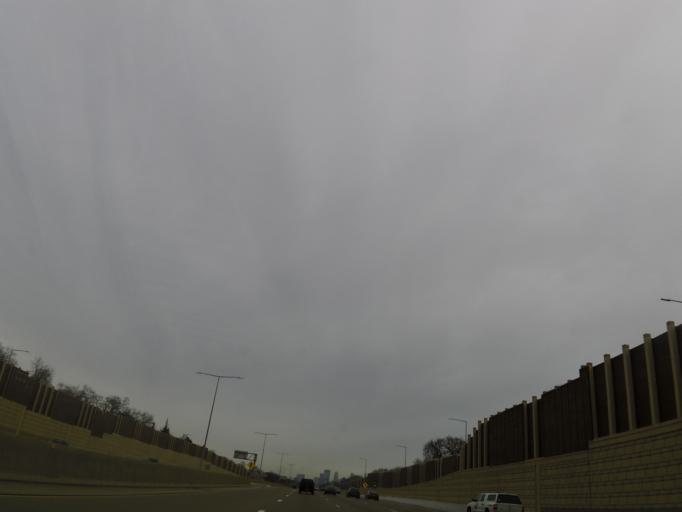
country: US
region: Minnesota
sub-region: Hennepin County
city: Richfield
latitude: 44.9209
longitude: -93.2744
